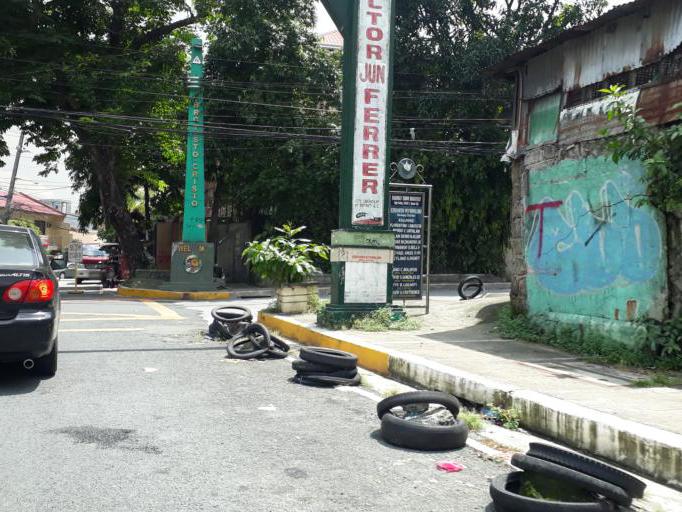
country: PH
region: Calabarzon
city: Bagong Pagasa
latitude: 14.6615
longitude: 121.0274
